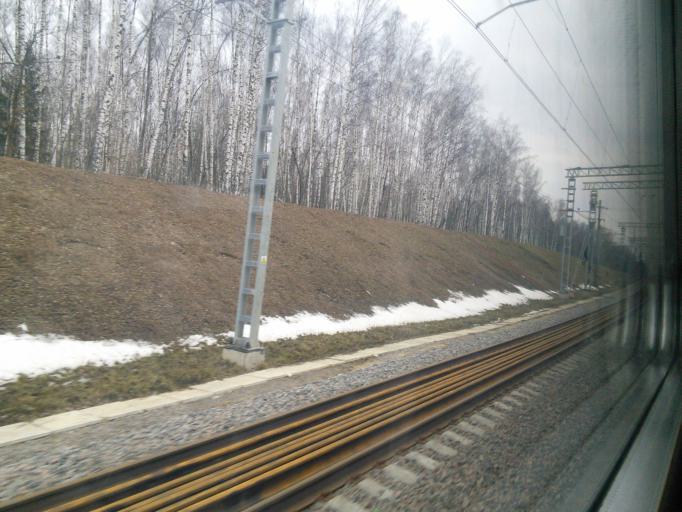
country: RU
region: Moskovskaya
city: Vostryakovo
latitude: 55.4338
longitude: 37.8520
